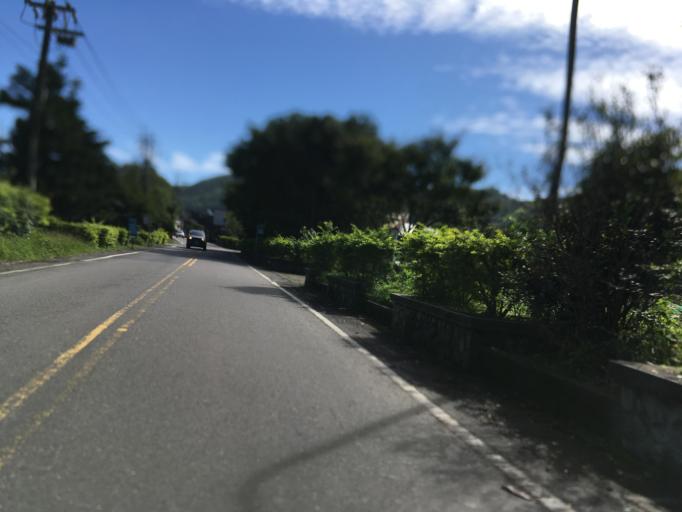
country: TW
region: Taiwan
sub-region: Yilan
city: Yilan
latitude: 24.6129
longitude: 121.8522
